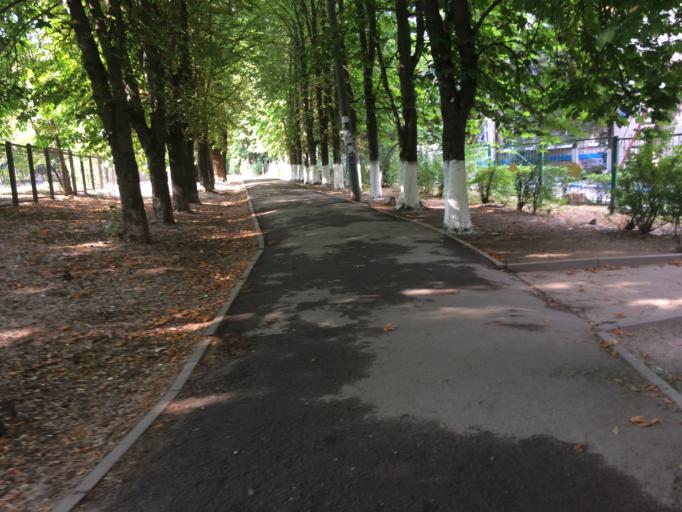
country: RU
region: Rostov
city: Rostov-na-Donu
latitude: 47.2100
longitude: 39.6421
